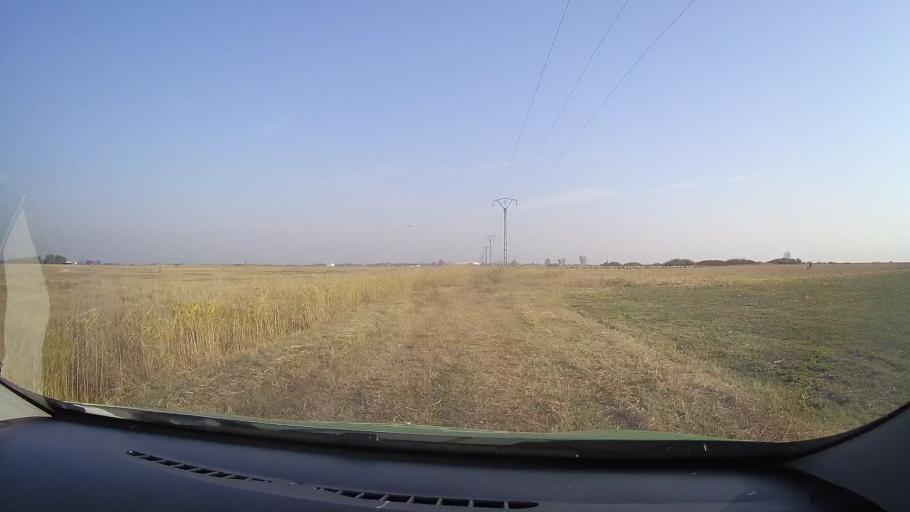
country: RO
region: Arad
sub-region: Comuna Pilu
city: Pilu
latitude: 46.5577
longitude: 21.3374
